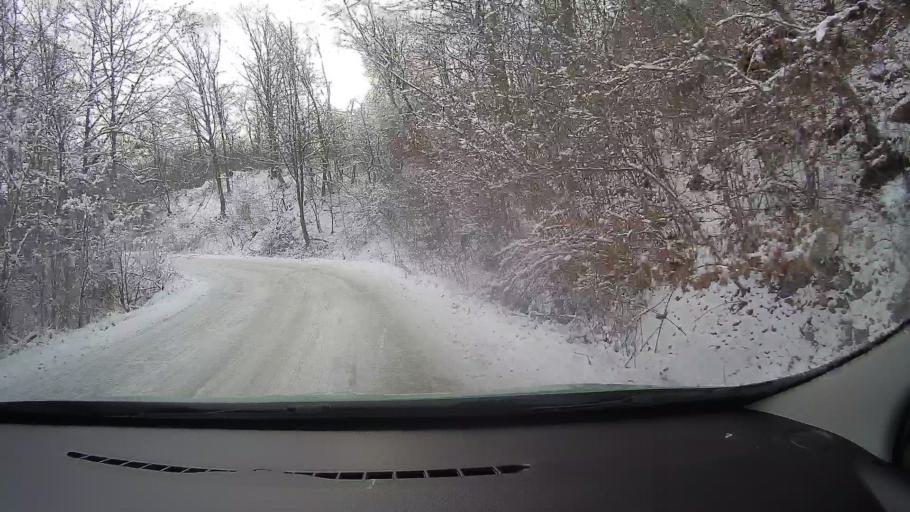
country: RO
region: Alba
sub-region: Comuna Almasu Mare
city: Almasu Mare
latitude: 46.0969
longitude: 23.1736
